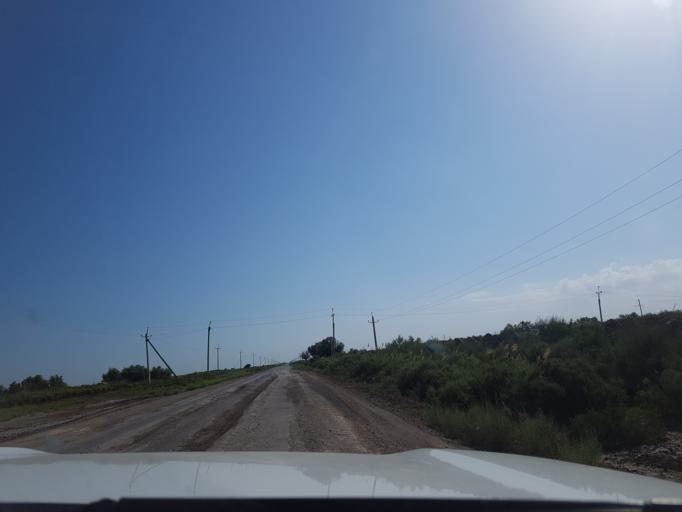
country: TM
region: Dasoguz
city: Koeneuergench
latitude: 42.0730
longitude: 58.8629
